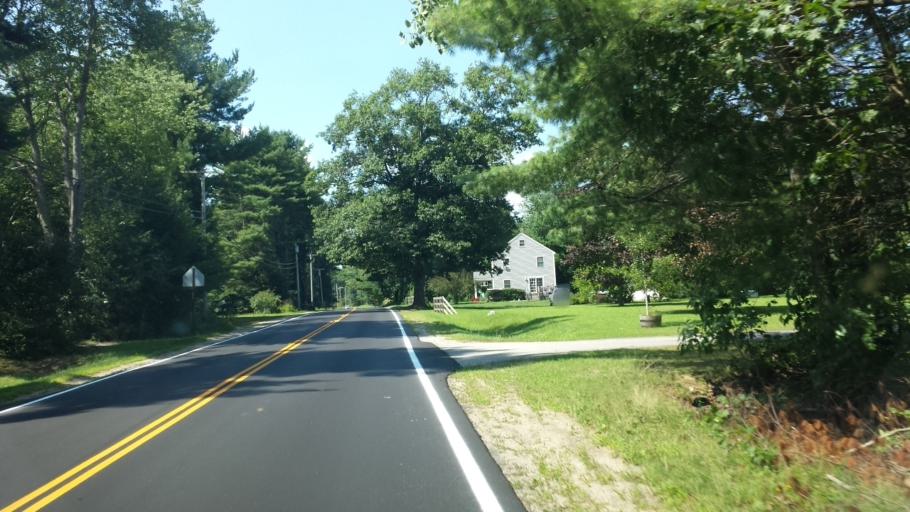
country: US
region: Maine
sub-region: York County
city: Arundel
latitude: 43.4166
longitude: -70.5014
